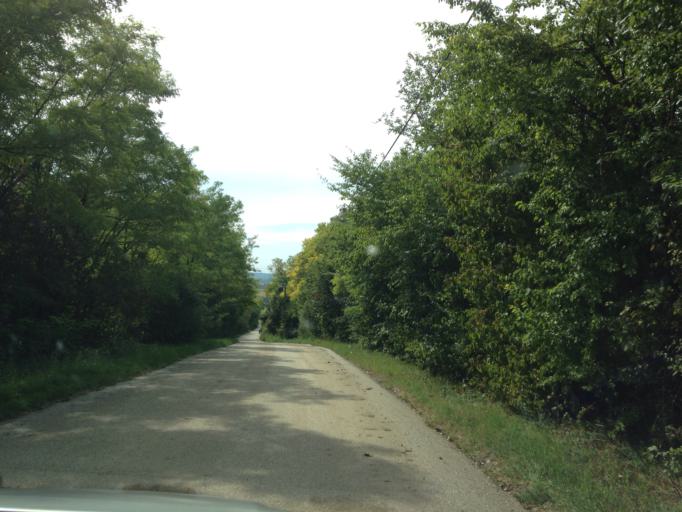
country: SK
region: Nitriansky
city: Svodin
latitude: 47.9142
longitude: 18.4304
